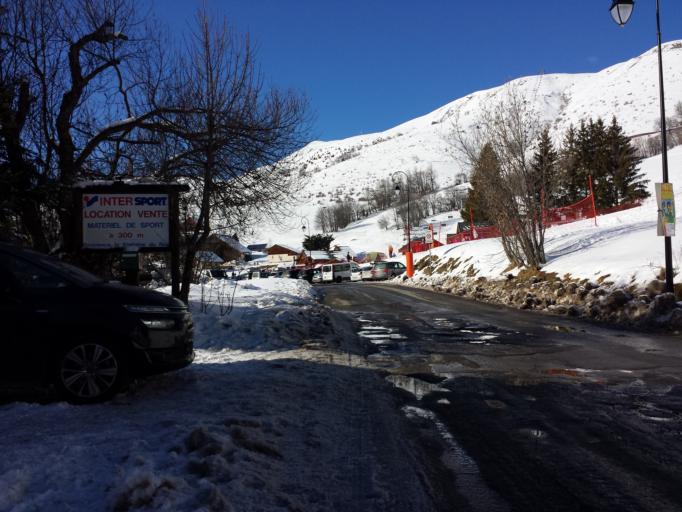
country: FR
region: Rhone-Alpes
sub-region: Departement de la Savoie
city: Saint-Jean-de-Maurienne
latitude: 45.2125
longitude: 6.2682
